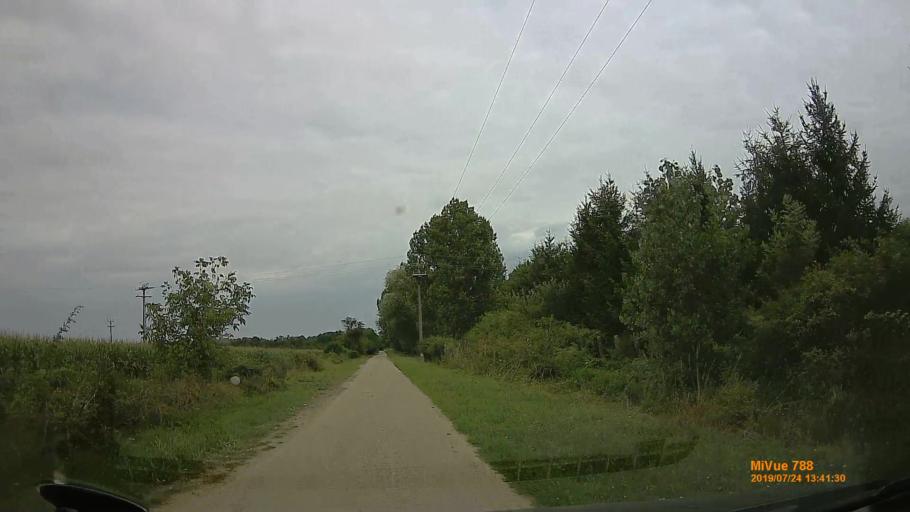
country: HU
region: Szabolcs-Szatmar-Bereg
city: Aranyosapati
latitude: 48.2586
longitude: 22.3165
